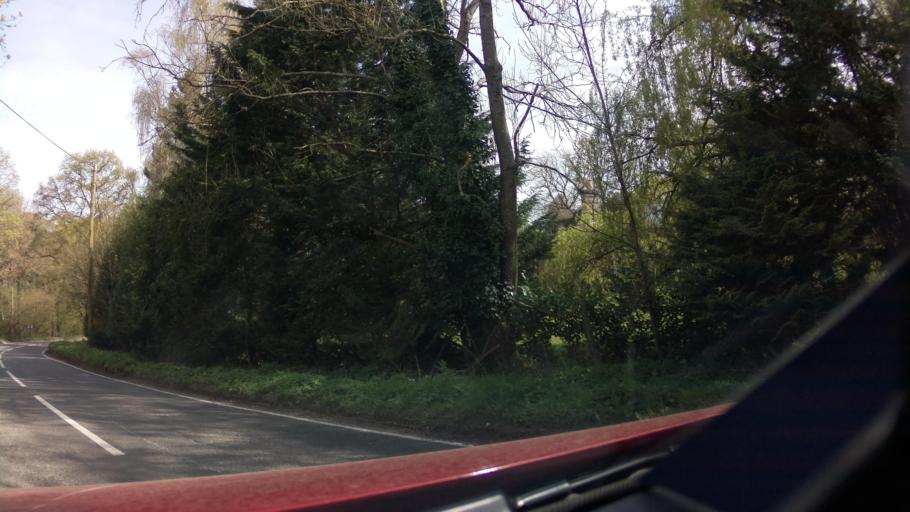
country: GB
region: England
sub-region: Hampshire
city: Compton
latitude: 51.0136
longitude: -1.3499
